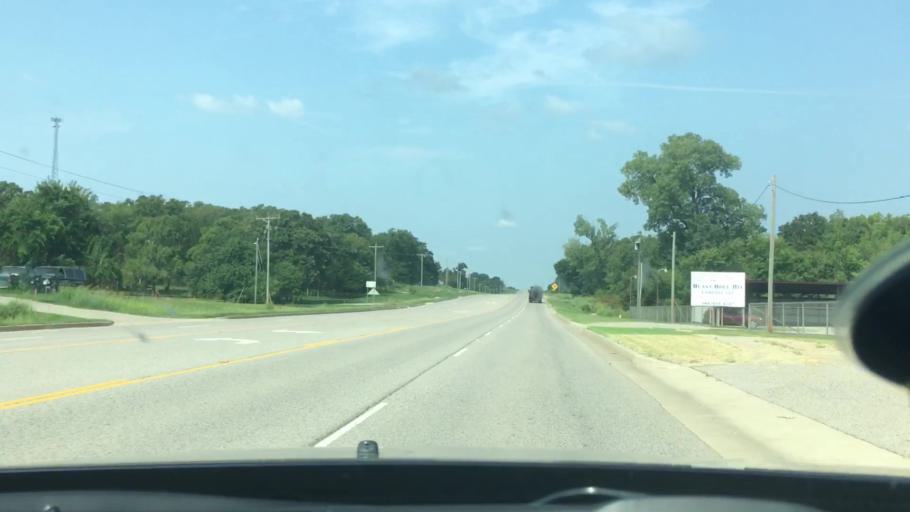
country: US
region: Oklahoma
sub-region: Bryan County
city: Calera
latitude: 33.9983
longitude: -96.5302
